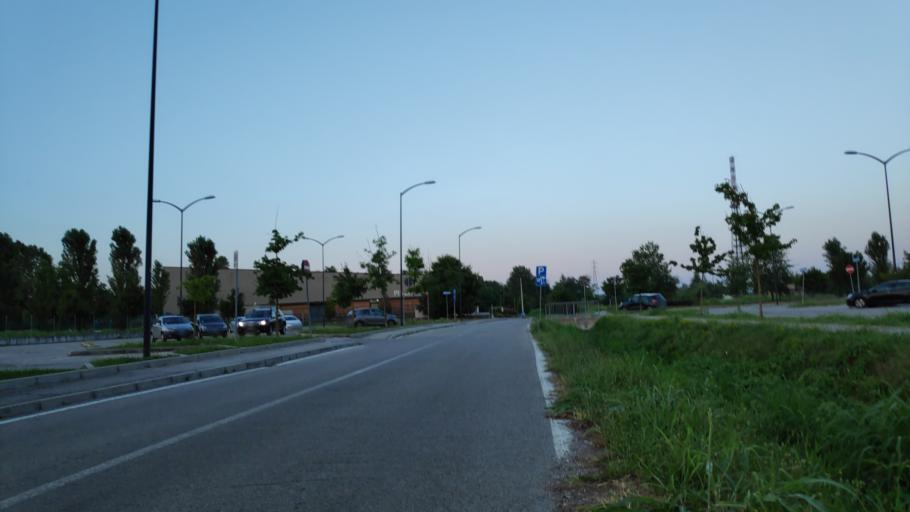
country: IT
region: Veneto
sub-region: Provincia di Treviso
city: Carbonera
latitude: 45.6702
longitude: 12.2674
